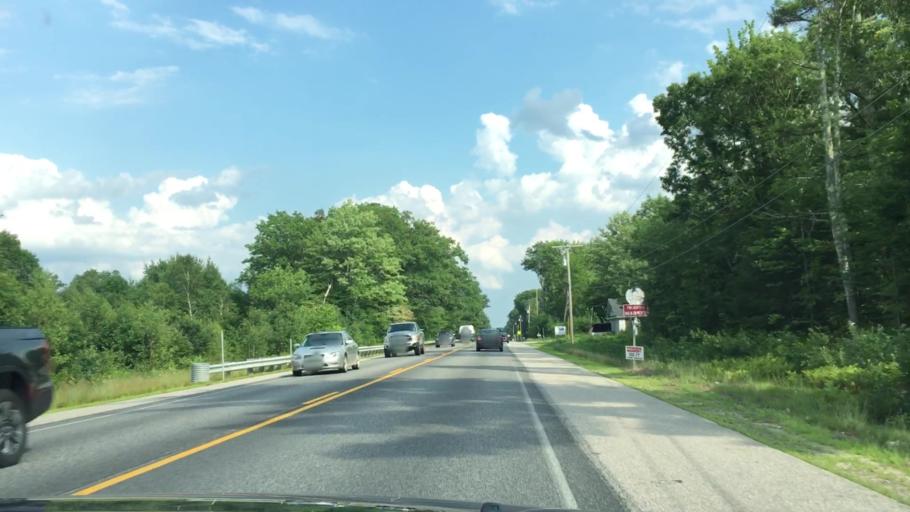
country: US
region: New Hampshire
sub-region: Strafford County
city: Farmington
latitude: 43.3985
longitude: -71.1048
